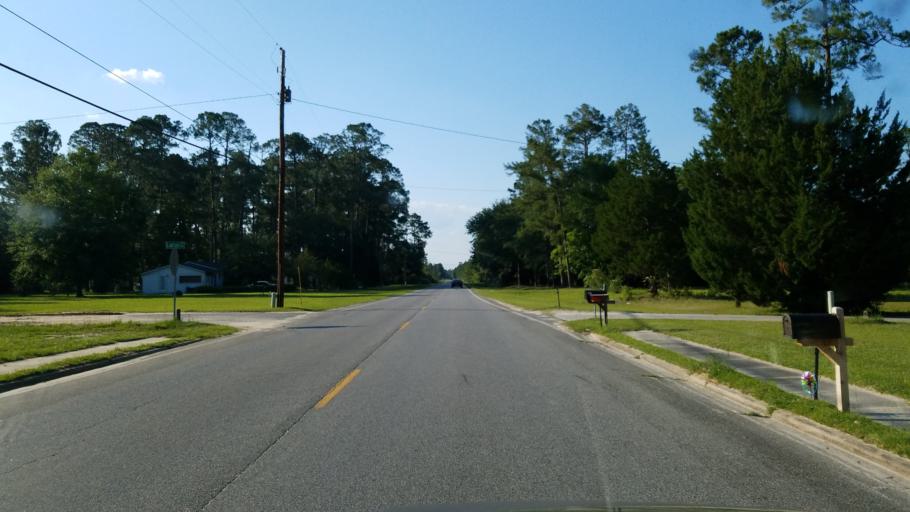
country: US
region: Georgia
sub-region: Lanier County
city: Lakeland
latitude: 30.9126
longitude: -83.0790
